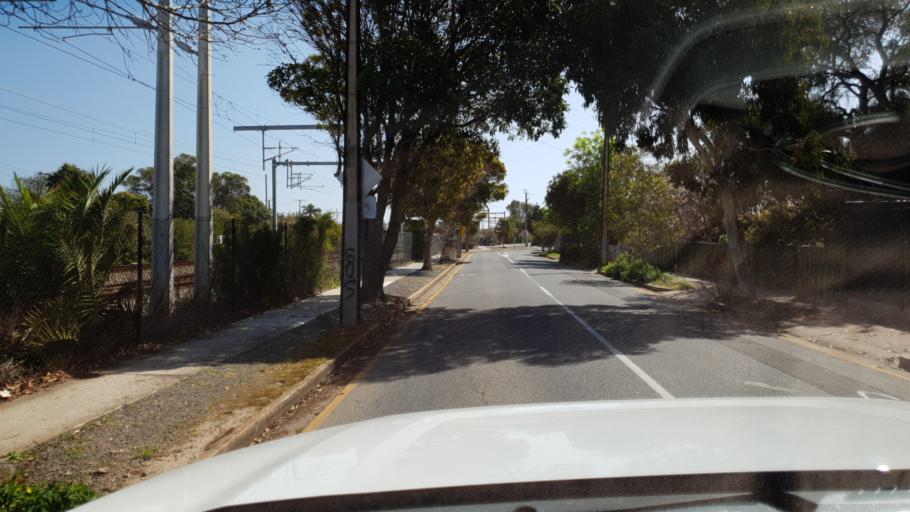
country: AU
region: South Australia
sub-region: Adelaide
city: Brighton
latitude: -35.0240
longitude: 138.5205
